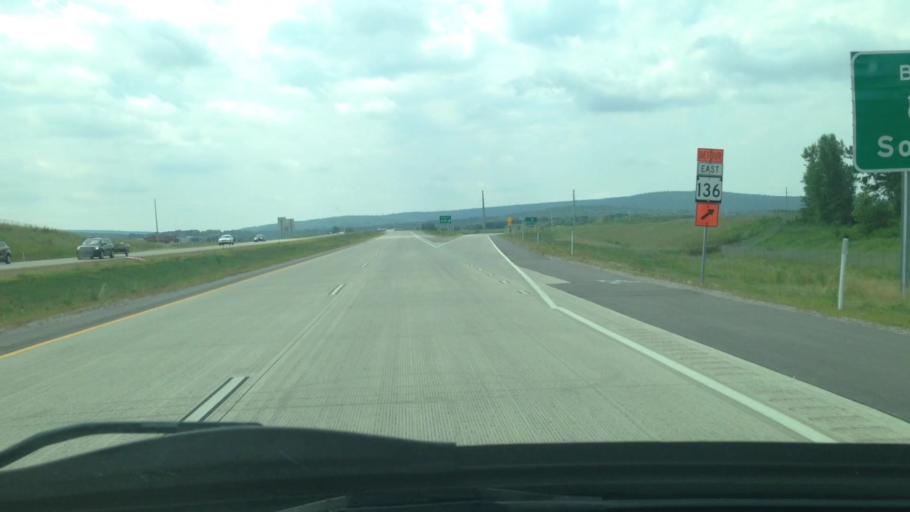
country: US
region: Wisconsin
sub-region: Sauk County
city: West Baraboo
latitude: 43.4651
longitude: -89.7774
